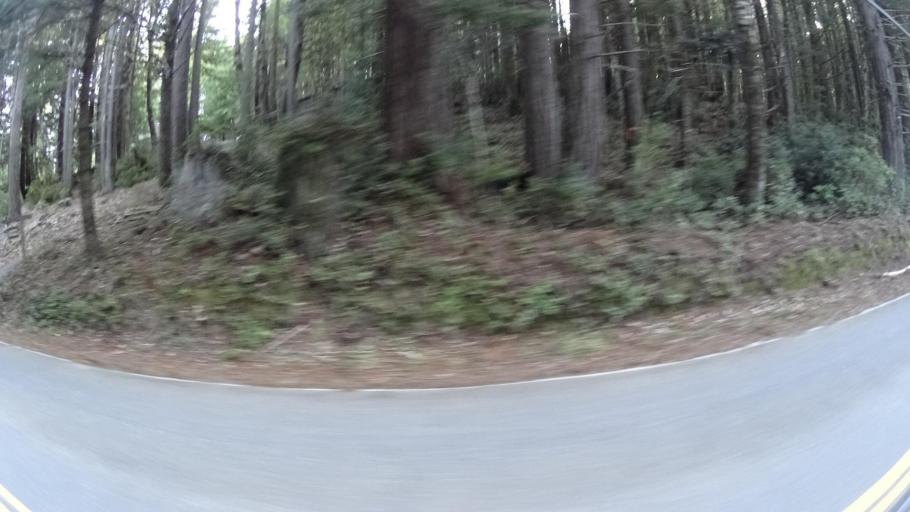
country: US
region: California
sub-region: Humboldt County
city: Bayside
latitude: 40.7595
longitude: -123.9933
